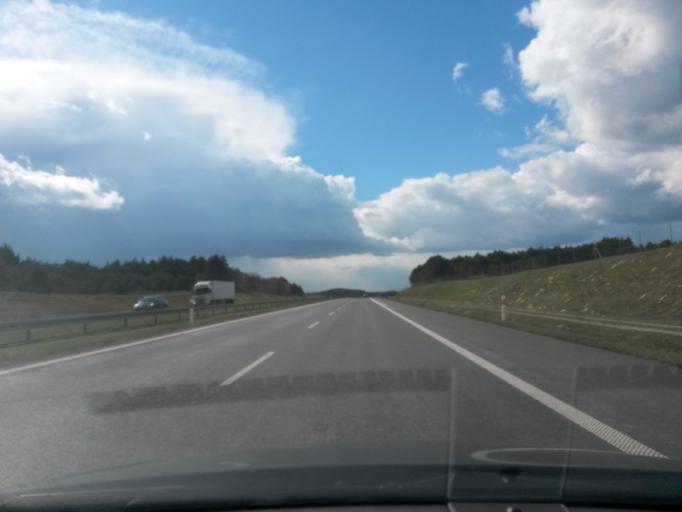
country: PL
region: Greater Poland Voivodeship
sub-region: Powiat kolski
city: Koscielec
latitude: 52.1416
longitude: 18.5509
